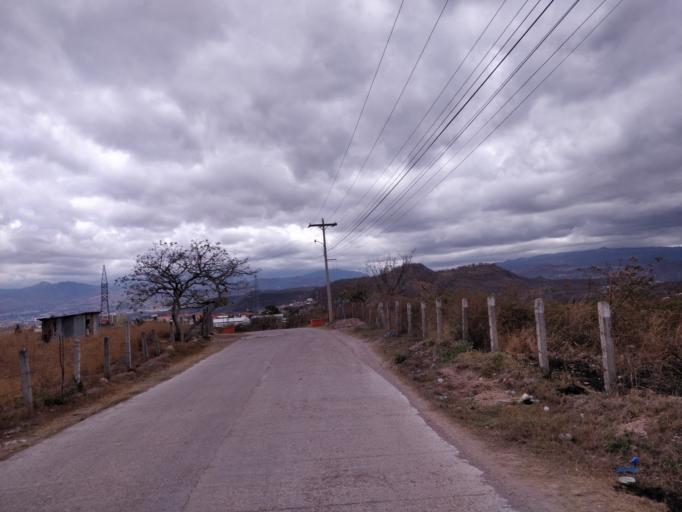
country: HN
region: Francisco Morazan
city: Yaguacire
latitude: 14.0342
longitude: -87.2448
